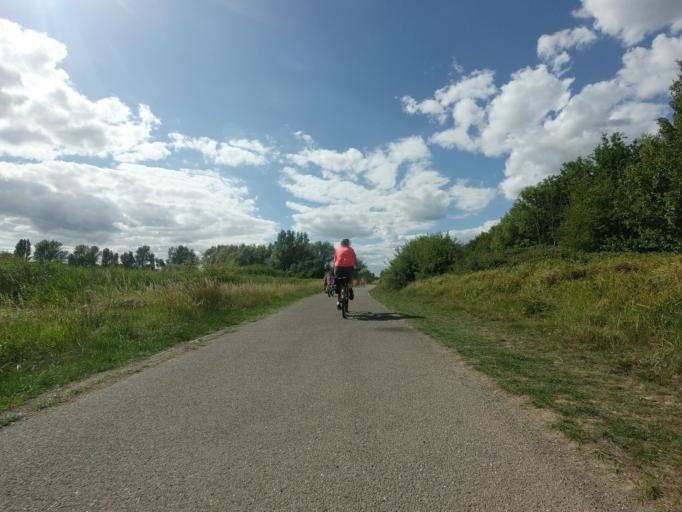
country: GB
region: England
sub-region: East Sussex
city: Eastbourne
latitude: 50.8046
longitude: 0.2853
